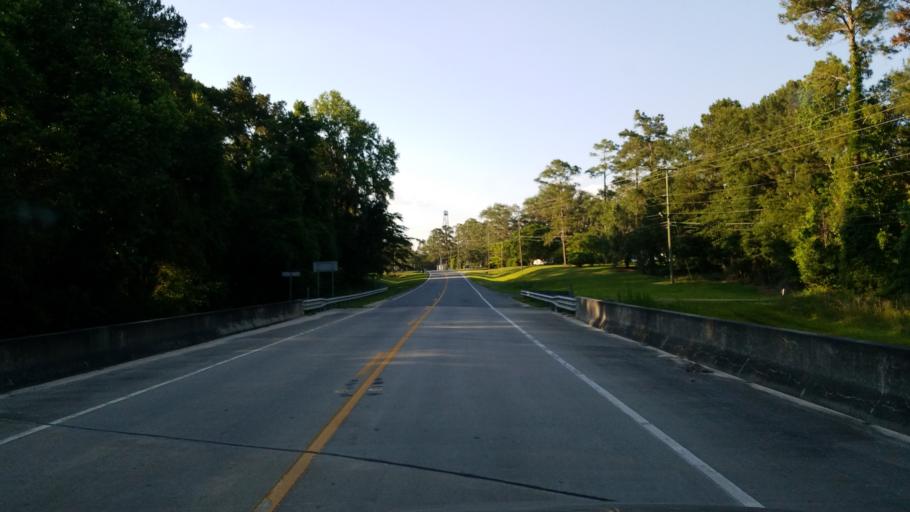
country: US
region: Georgia
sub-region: Lanier County
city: Lakeland
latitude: 31.0495
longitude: -83.0696
